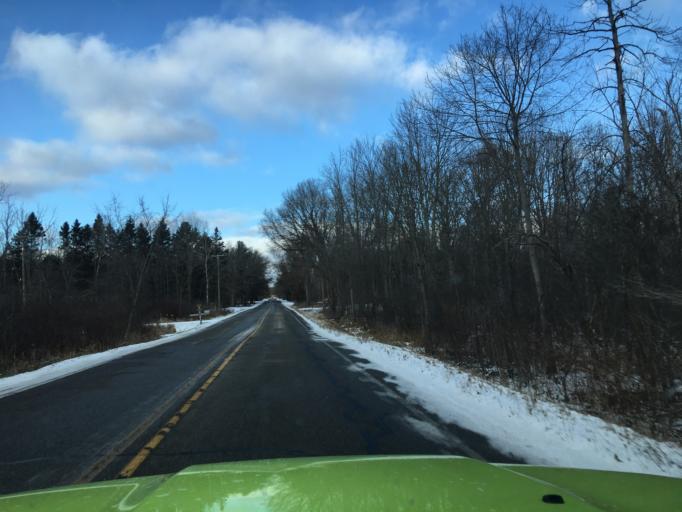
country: US
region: Michigan
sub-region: Montcalm County
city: Greenville
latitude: 43.1951
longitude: -85.2828
